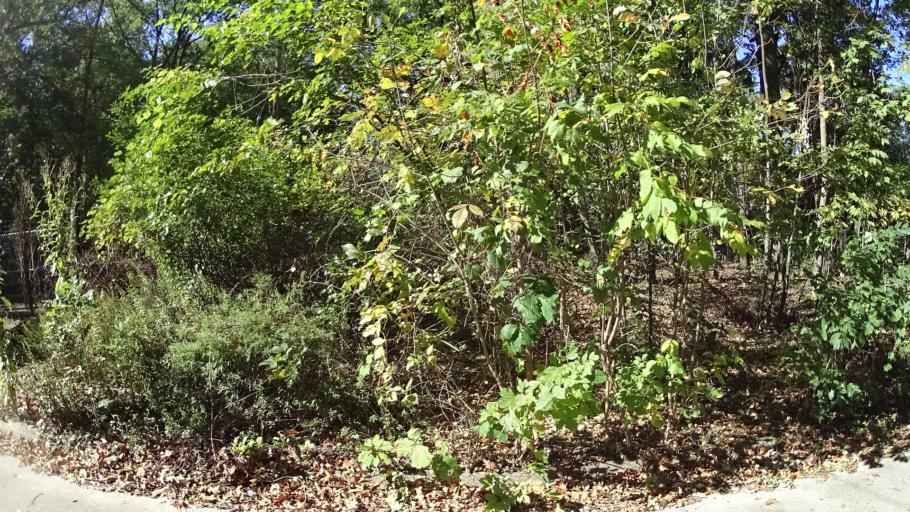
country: US
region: Ohio
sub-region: Lorain County
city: Lorain
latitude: 41.4341
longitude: -82.1745
